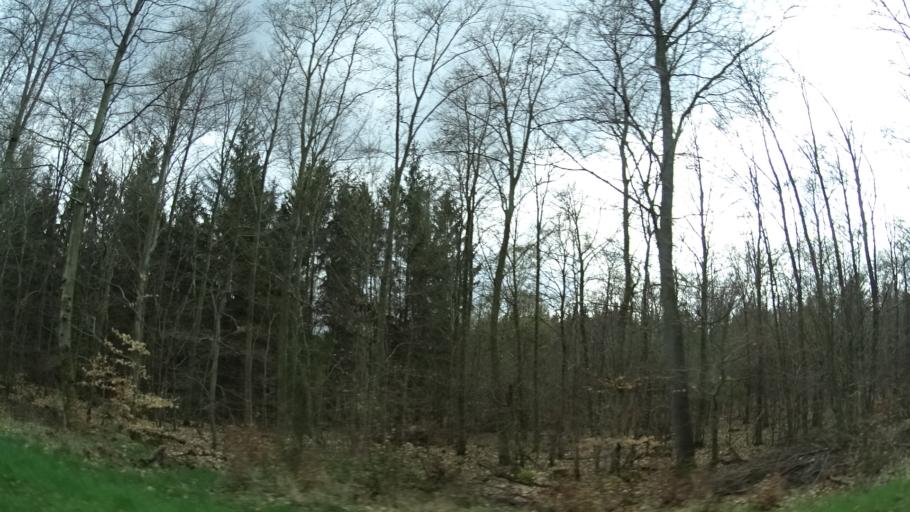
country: DE
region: Rheinland-Pfalz
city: Seesbach
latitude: 49.8700
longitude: 7.5633
